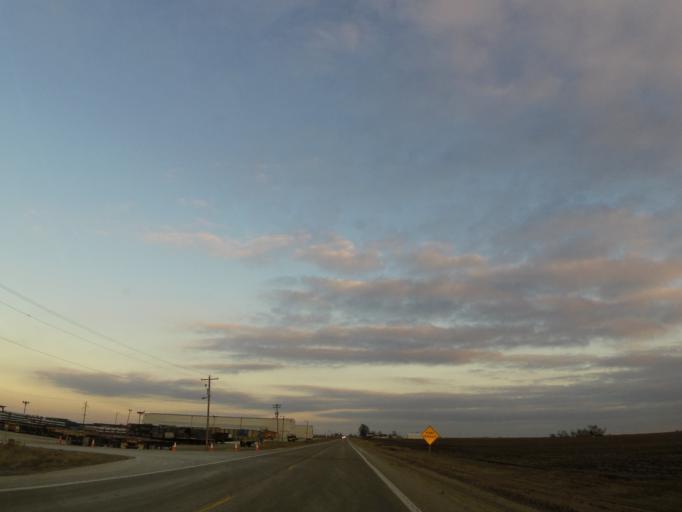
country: US
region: Illinois
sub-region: Woodford County
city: El Paso
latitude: 40.7380
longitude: -88.9799
